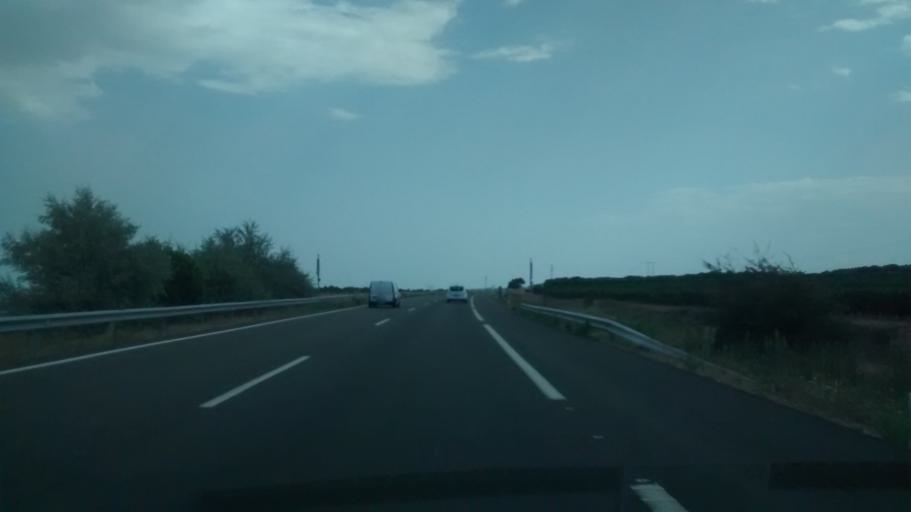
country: ES
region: La Rioja
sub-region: Provincia de La Rioja
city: Calahorra
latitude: 42.2788
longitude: -1.9381
